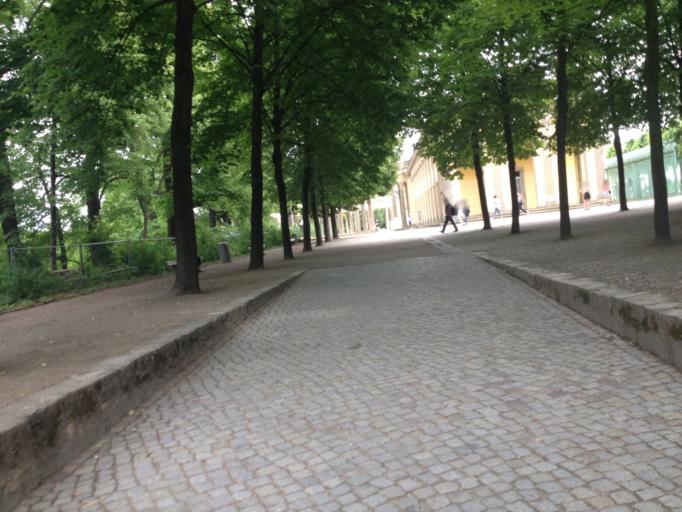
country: DE
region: Brandenburg
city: Potsdam
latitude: 52.4043
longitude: 13.0366
